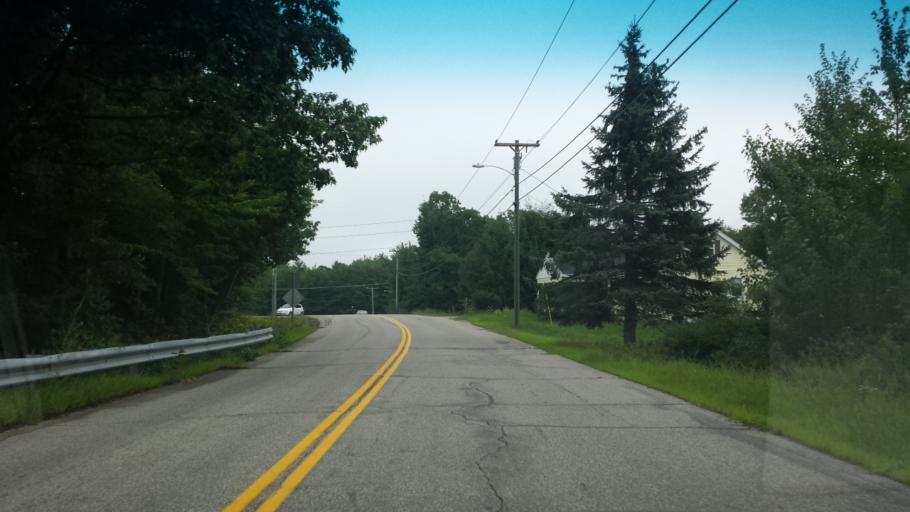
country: US
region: Maine
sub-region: York County
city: Biddeford
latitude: 43.4744
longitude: -70.4962
